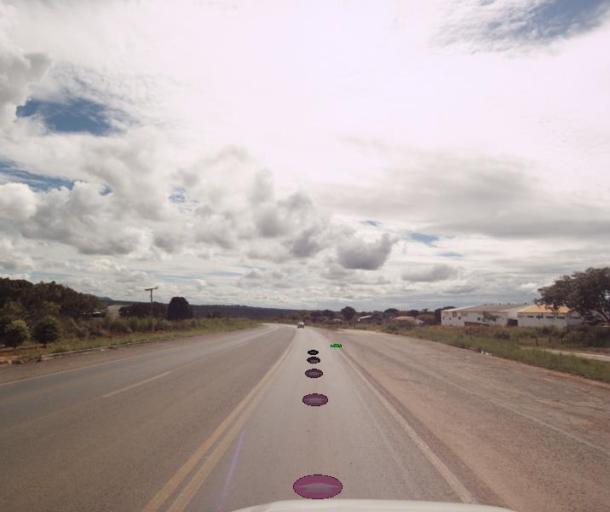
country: BR
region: Goias
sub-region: Uruacu
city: Uruacu
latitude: -14.5141
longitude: -49.1500
